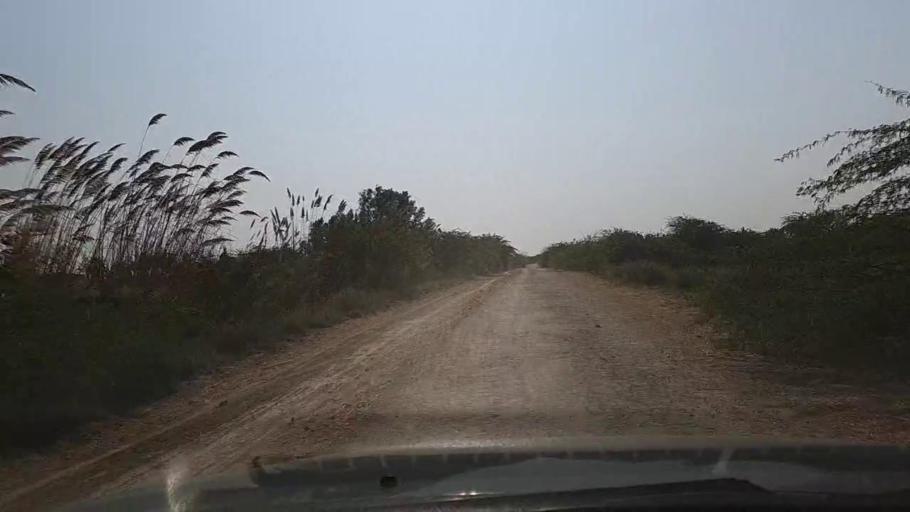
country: PK
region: Sindh
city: Mirpur Sakro
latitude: 24.3951
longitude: 67.6659
